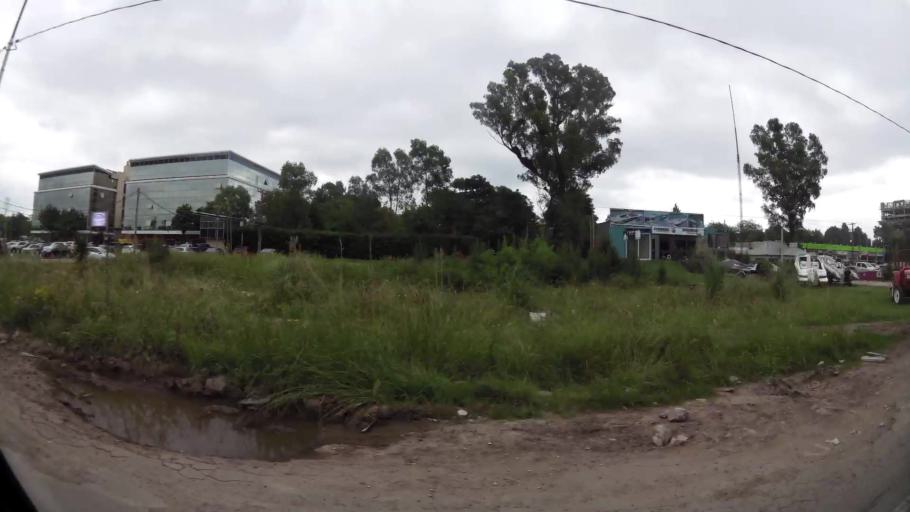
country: AR
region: Buenos Aires
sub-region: Partido de Ezeiza
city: Ezeiza
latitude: -34.8846
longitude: -58.5049
